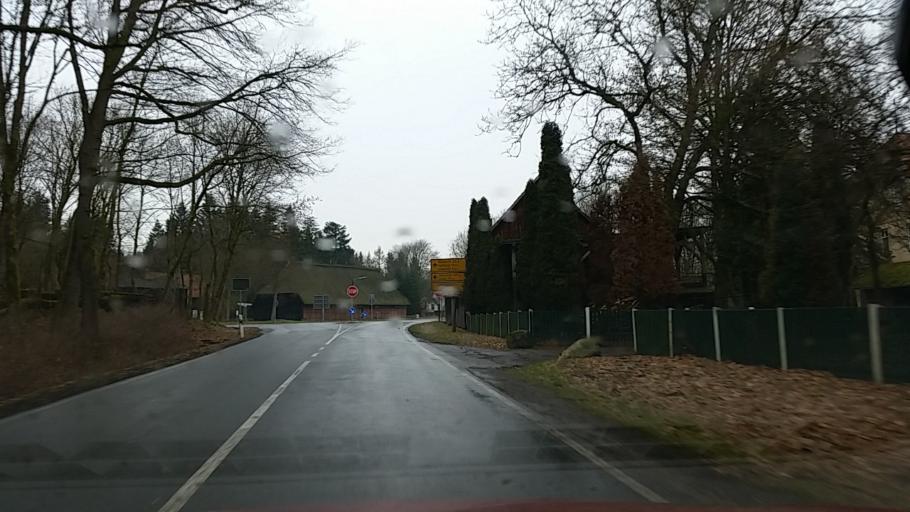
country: DE
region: Lower Saxony
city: Unterluss
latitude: 52.7916
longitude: 10.3855
